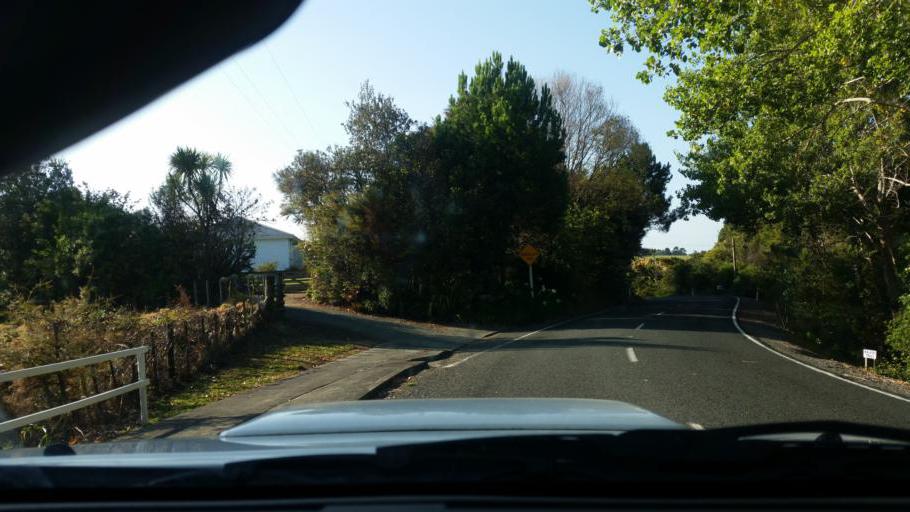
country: NZ
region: Northland
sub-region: Whangarei
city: Ruakaka
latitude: -36.1089
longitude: 174.2293
